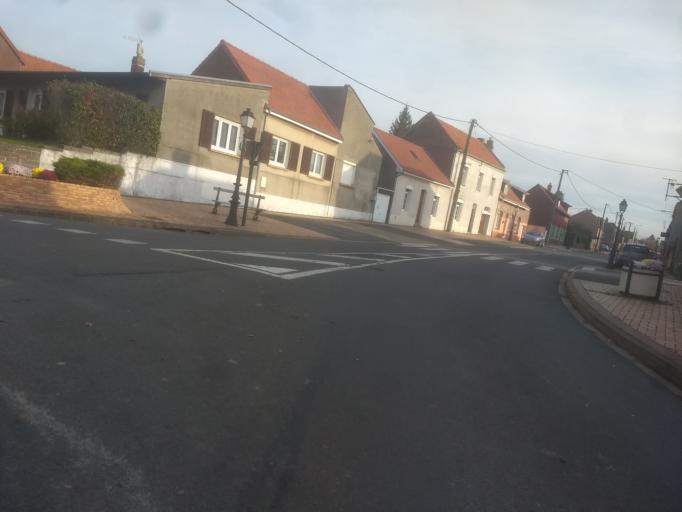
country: FR
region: Nord-Pas-de-Calais
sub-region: Departement du Pas-de-Calais
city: Agny
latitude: 50.2608
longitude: 2.7588
